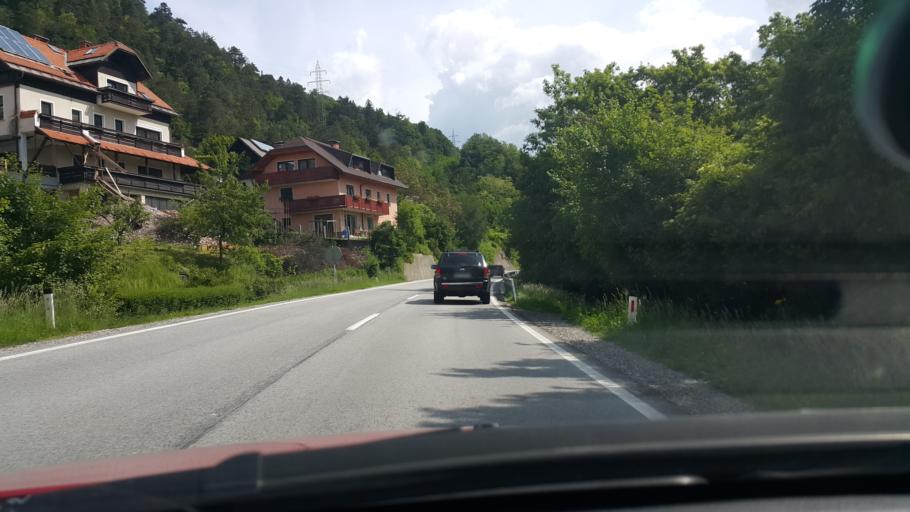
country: SI
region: Trzic
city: Bistrica pri Trzicu
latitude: 46.3588
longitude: 14.2964
